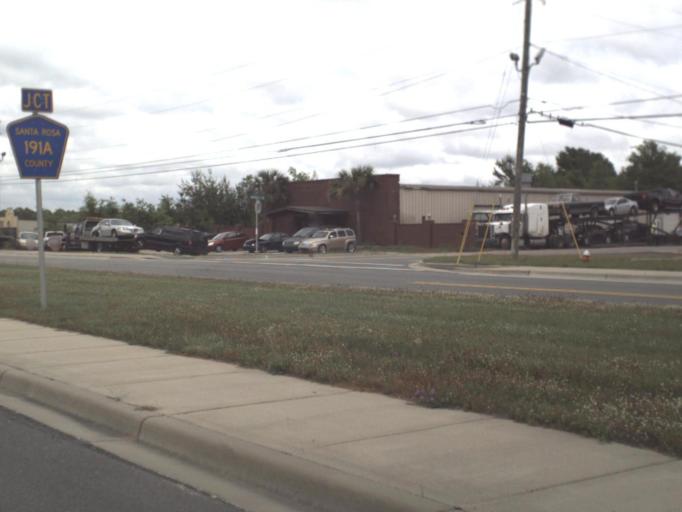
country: US
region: Florida
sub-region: Santa Rosa County
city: Bagdad
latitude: 30.5833
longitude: -87.0860
